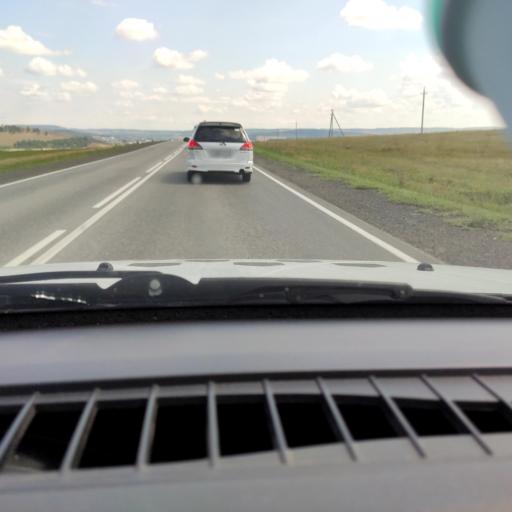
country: RU
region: Bashkortostan
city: Verkhniye Kigi
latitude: 55.4276
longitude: 58.5575
